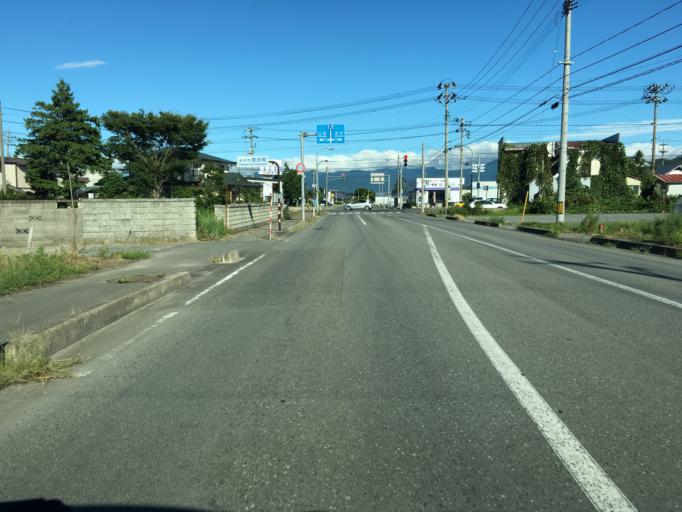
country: JP
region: Yamagata
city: Yonezawa
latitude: 37.9558
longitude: 140.1243
